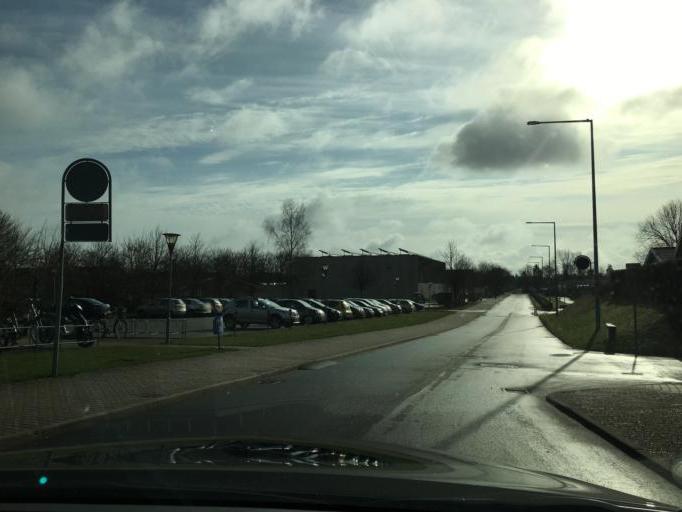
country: DK
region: South Denmark
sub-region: Kolding Kommune
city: Kolding
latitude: 55.5020
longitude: 9.4449
